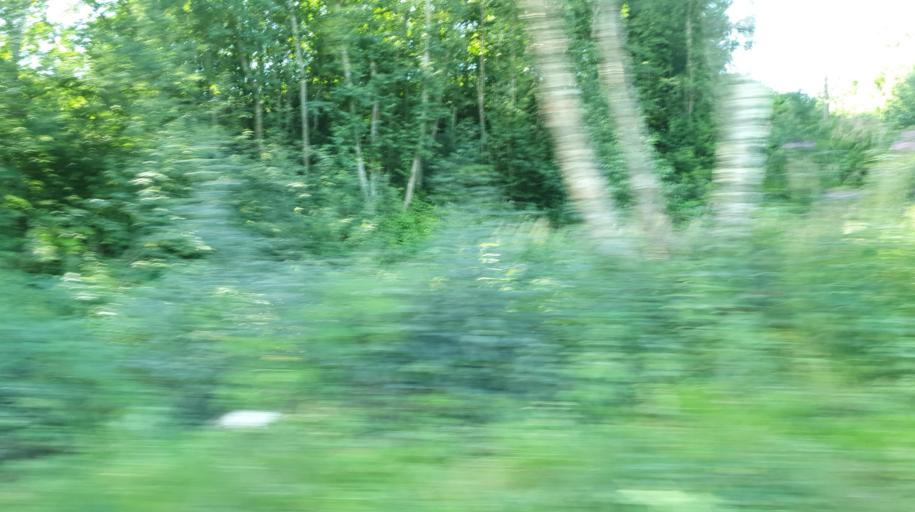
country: NO
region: Nord-Trondelag
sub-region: Levanger
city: Skogn
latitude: 63.6995
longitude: 11.2376
